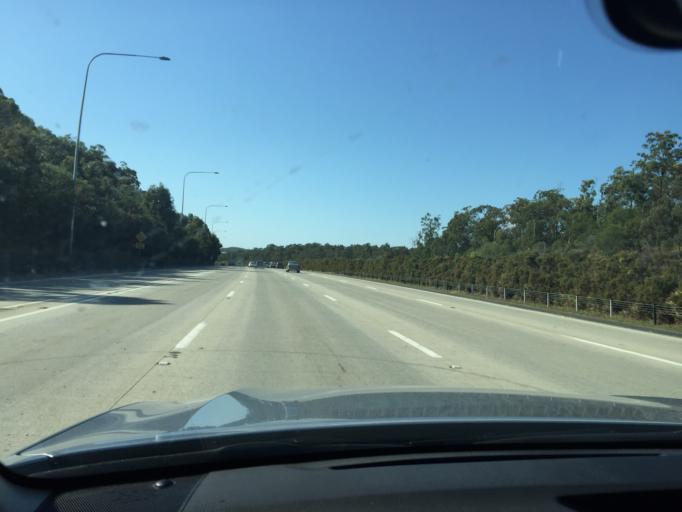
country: AU
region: Queensland
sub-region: Gold Coast
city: Ormeau Hills
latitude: -27.8071
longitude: 153.2667
